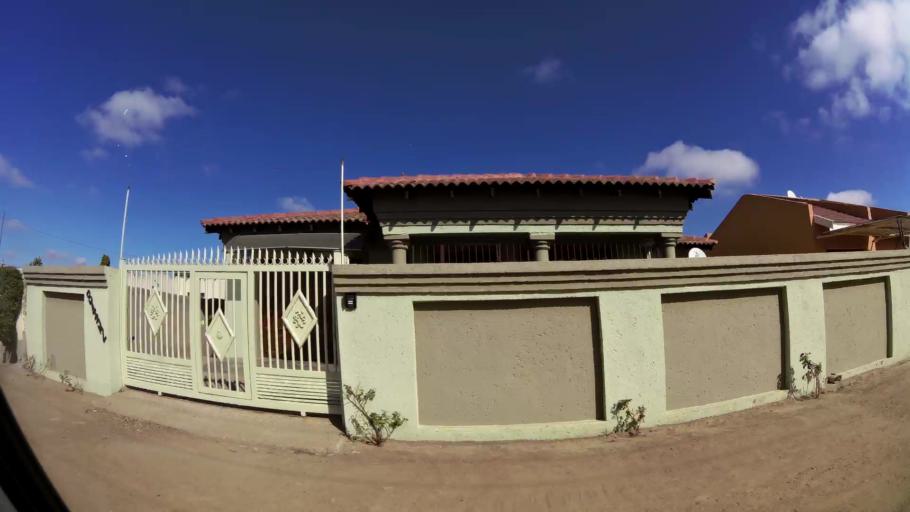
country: ZA
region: Limpopo
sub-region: Capricorn District Municipality
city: Polokwane
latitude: -23.8633
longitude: 29.3825
